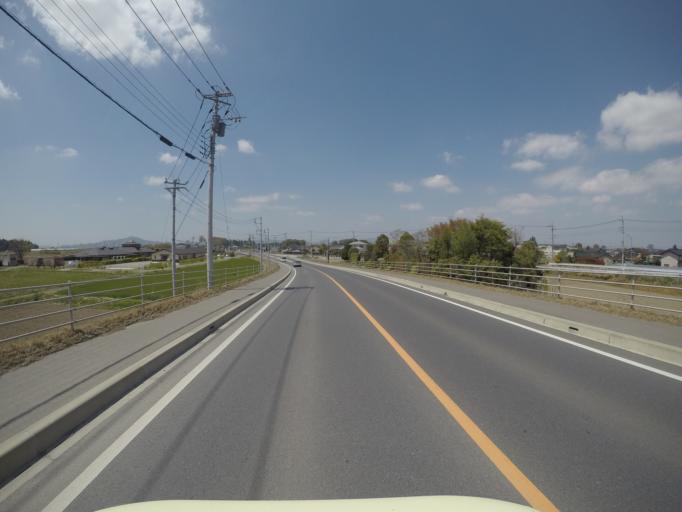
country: JP
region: Tochigi
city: Mibu
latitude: 36.3908
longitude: 139.7927
